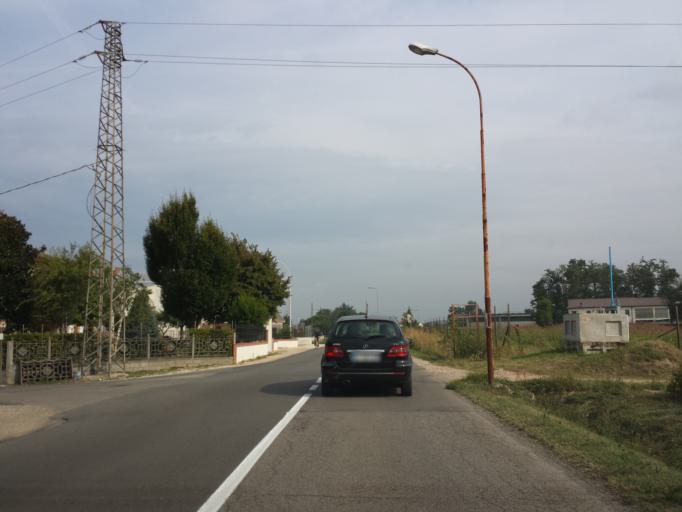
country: IT
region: Veneto
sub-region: Provincia di Verona
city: San Gregorio
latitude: 45.3501
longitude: 11.2908
